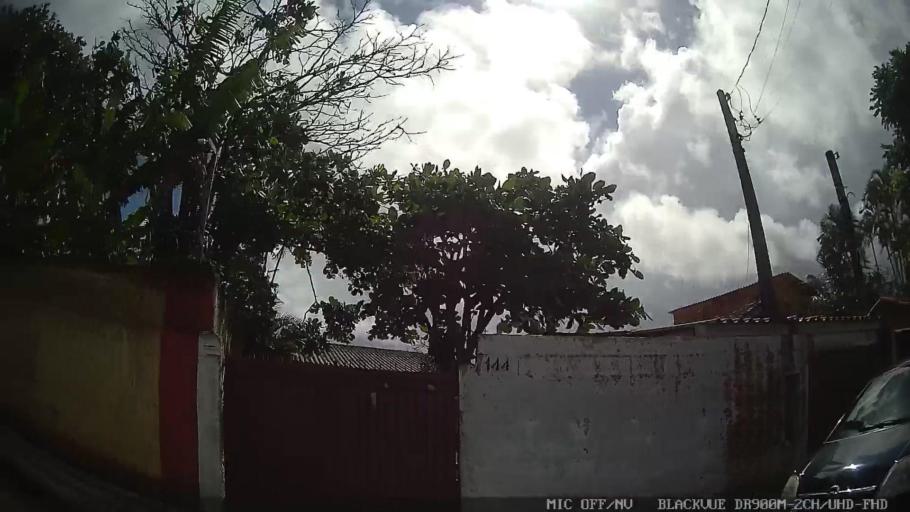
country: BR
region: Sao Paulo
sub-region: Itanhaem
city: Itanhaem
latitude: -24.1929
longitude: -46.8095
